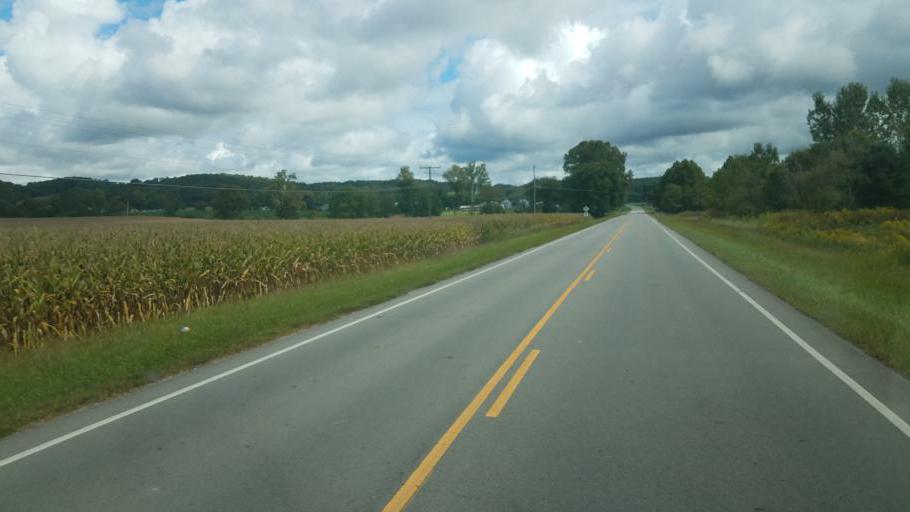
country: US
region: Ohio
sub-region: Scioto County
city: Sciotodale
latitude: 38.8669
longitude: -82.8511
